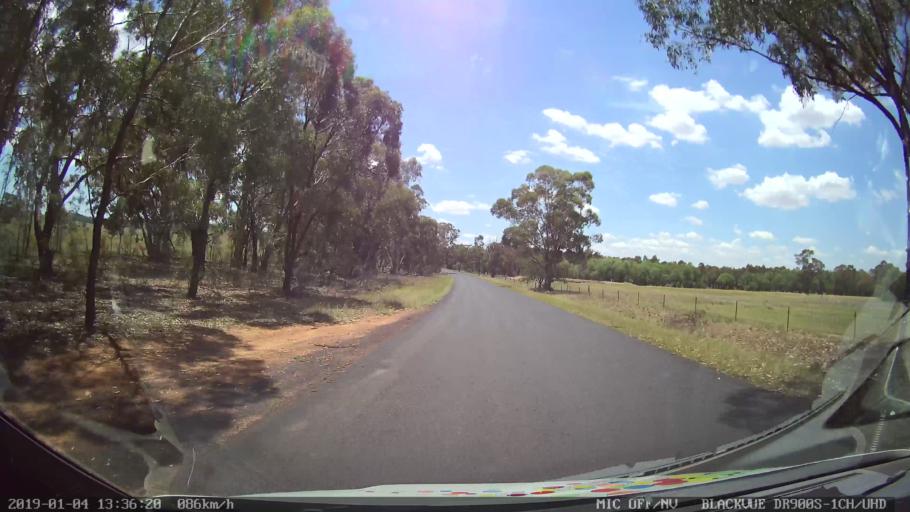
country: AU
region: New South Wales
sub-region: Dubbo Municipality
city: Dubbo
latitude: -32.5621
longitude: 148.5373
